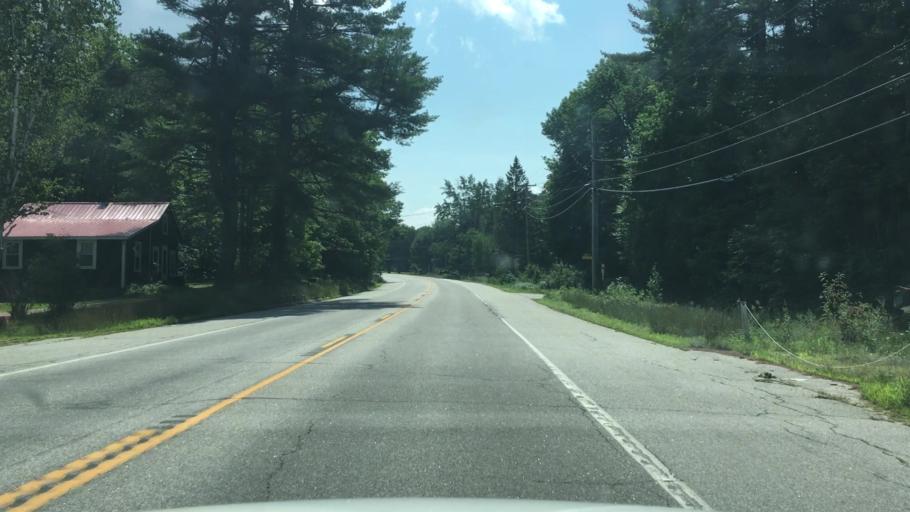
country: US
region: Maine
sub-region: Cumberland County
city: Raymond
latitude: 43.9304
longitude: -70.5377
